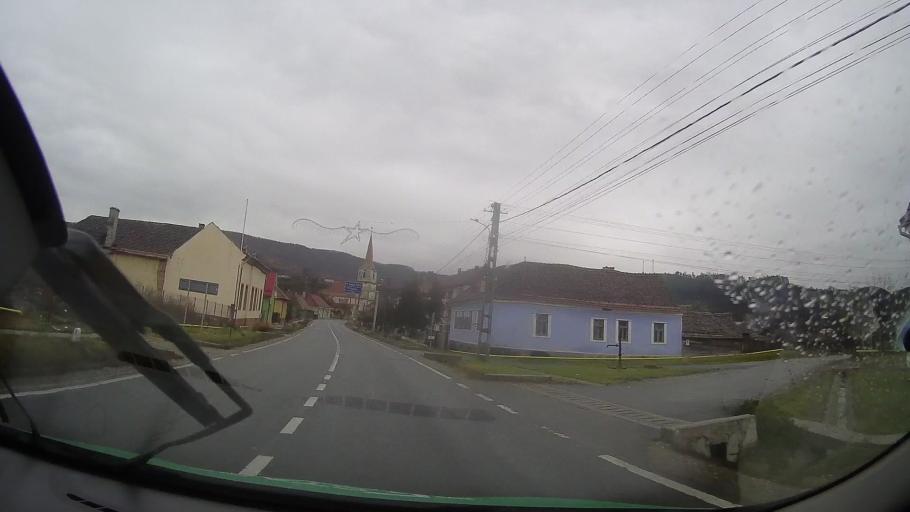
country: RO
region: Bistrita-Nasaud
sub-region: Comuna Teaca
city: Teaca
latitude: 46.9119
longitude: 24.5041
